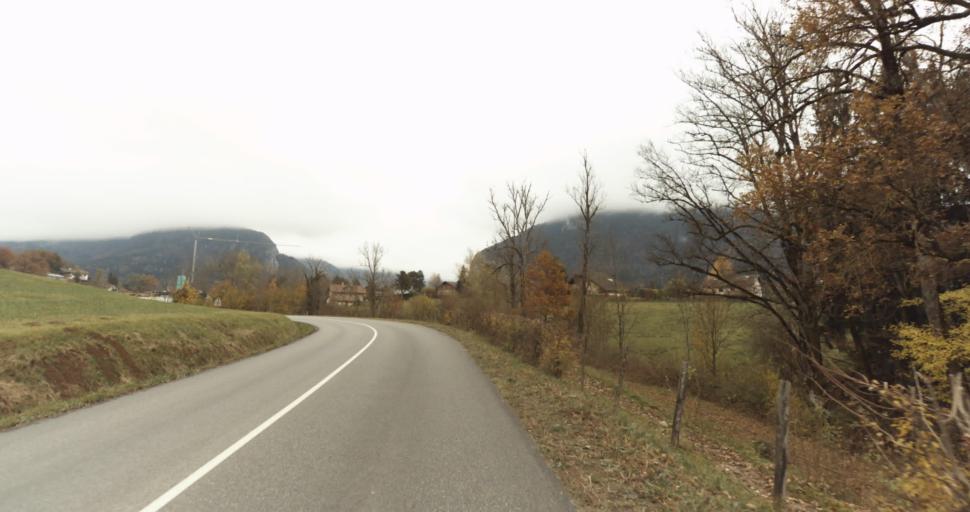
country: FR
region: Rhone-Alpes
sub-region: Departement de la Haute-Savoie
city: Thorens-Glieres
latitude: 45.9974
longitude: 6.2361
